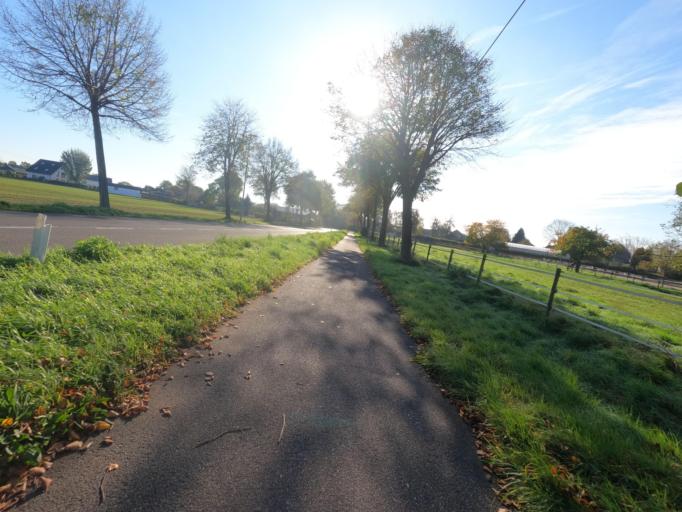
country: DE
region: North Rhine-Westphalia
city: Erkelenz
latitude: 51.0669
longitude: 6.3268
